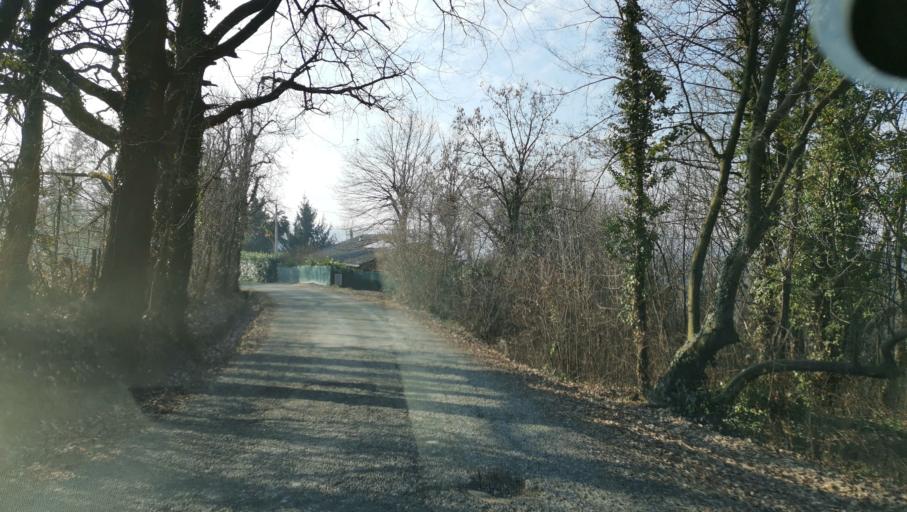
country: IT
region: Piedmont
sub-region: Provincia di Torino
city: Rivalba
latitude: 45.1261
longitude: 7.8938
